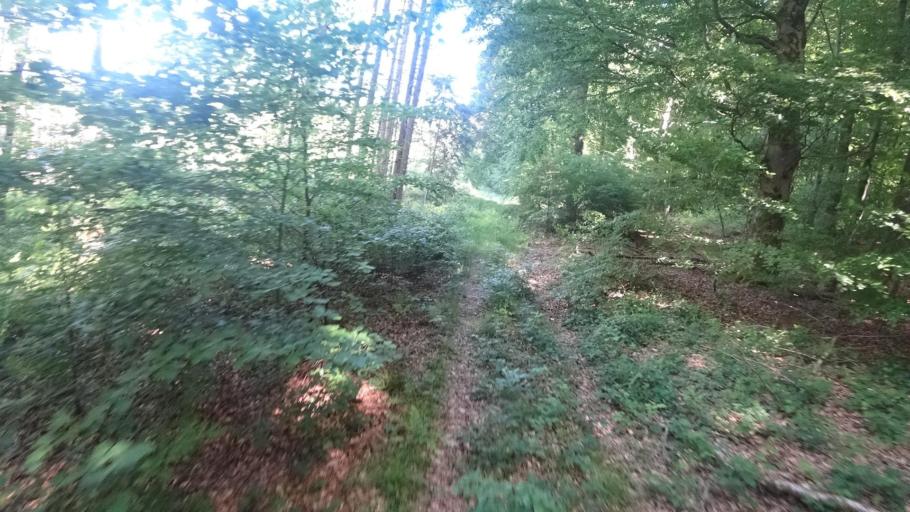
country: DE
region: Rheinland-Pfalz
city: Sorth
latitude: 50.7033
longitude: 7.6965
